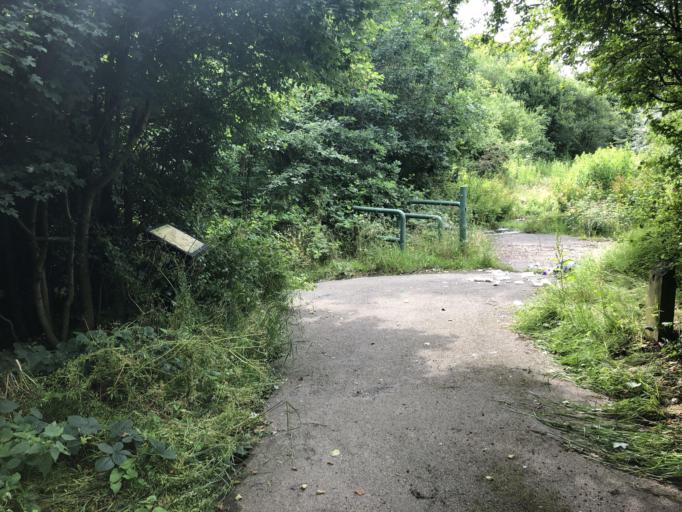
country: GB
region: England
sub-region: Walsall
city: Walsall
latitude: 52.5961
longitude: -1.9771
